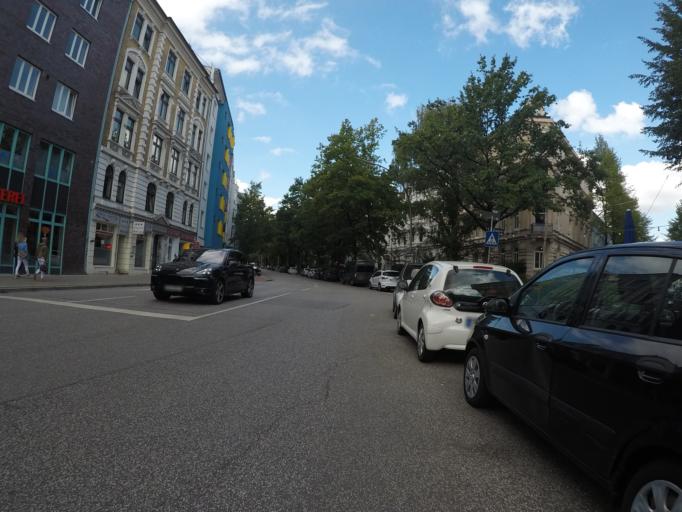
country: DE
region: Hamburg
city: Altona
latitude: 53.5553
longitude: 9.9263
